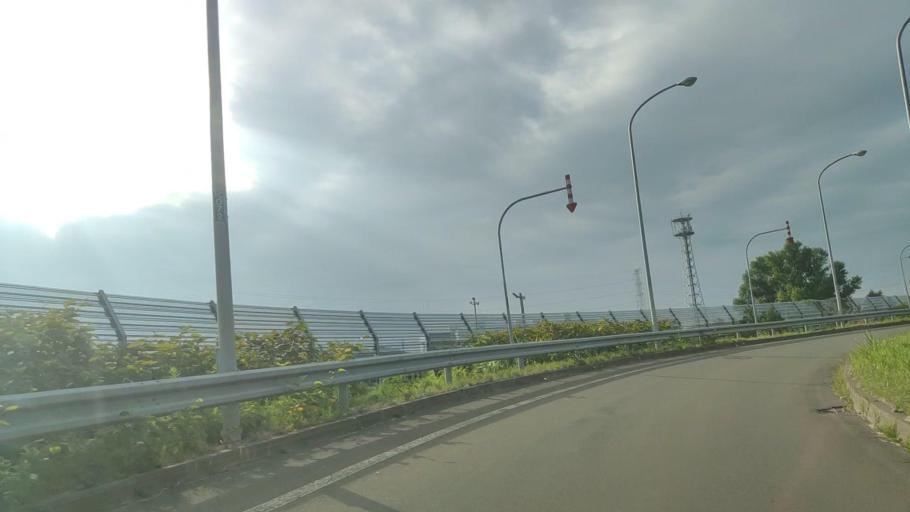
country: JP
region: Hokkaido
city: Ishikari
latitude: 43.1829
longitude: 141.3216
